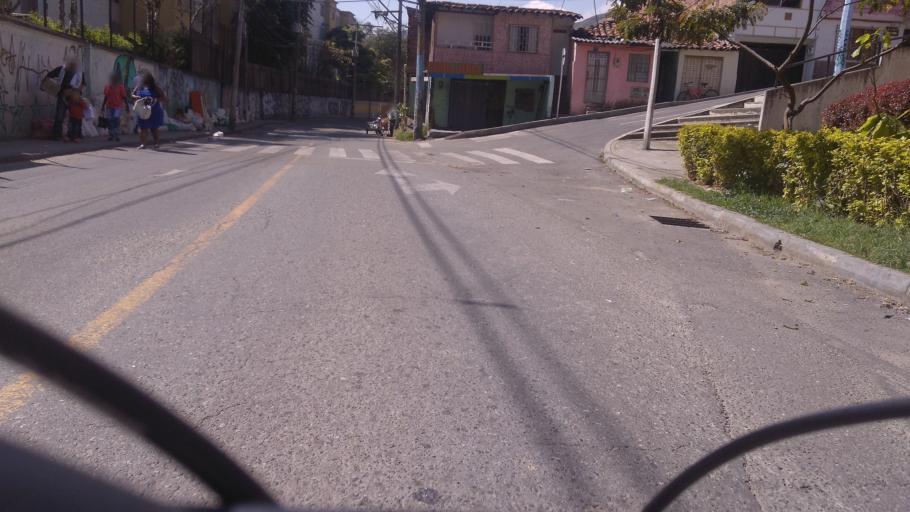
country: CO
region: Antioquia
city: Itagui
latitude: 6.2281
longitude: -75.6052
